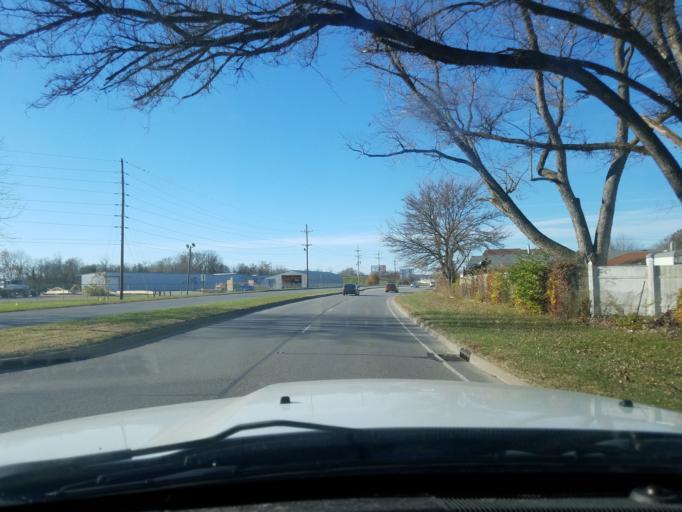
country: US
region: Indiana
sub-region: Clark County
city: Clarksville
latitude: 38.2930
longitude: -85.7681
